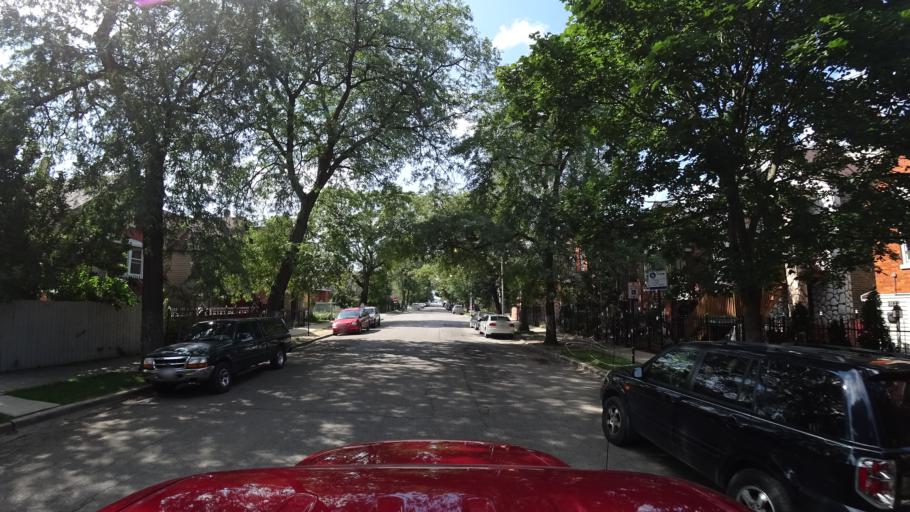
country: US
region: Illinois
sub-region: Cook County
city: Cicero
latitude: 41.8358
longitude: -87.7170
